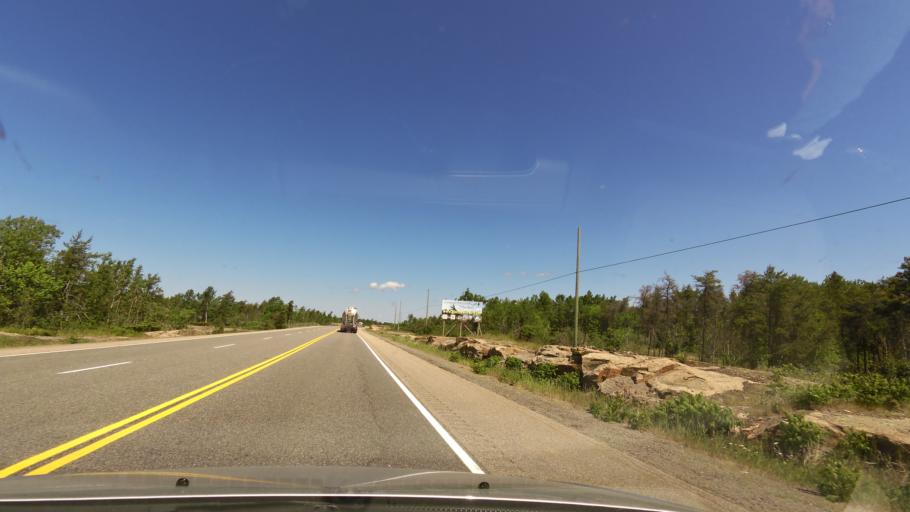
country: CA
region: Ontario
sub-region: Parry Sound District
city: Parry Sound
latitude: 45.7613
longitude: -80.4936
